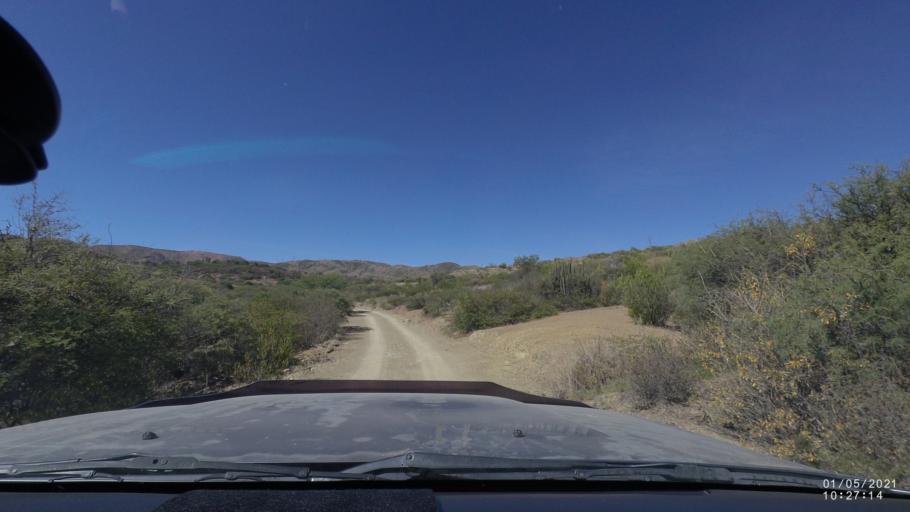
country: BO
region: Cochabamba
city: Capinota
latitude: -17.5839
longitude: -66.1913
